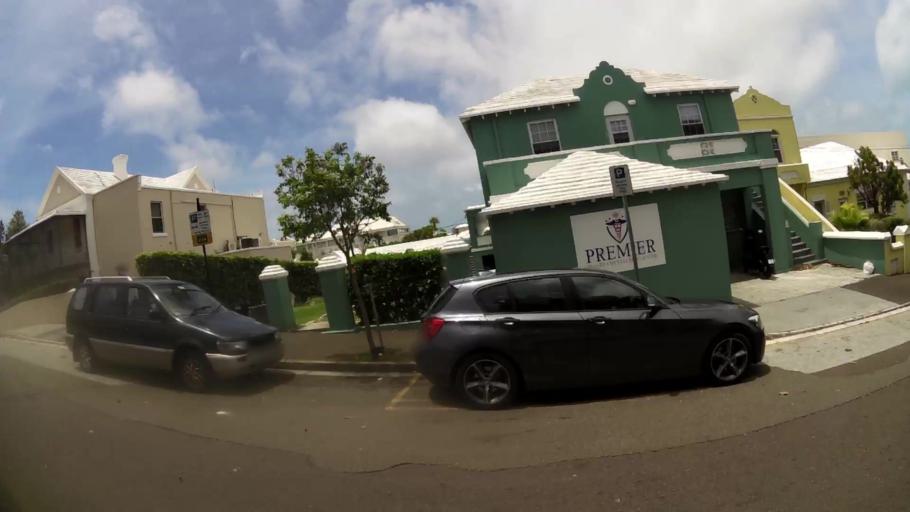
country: BM
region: Hamilton city
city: Hamilton
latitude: 32.2958
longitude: -64.7790
